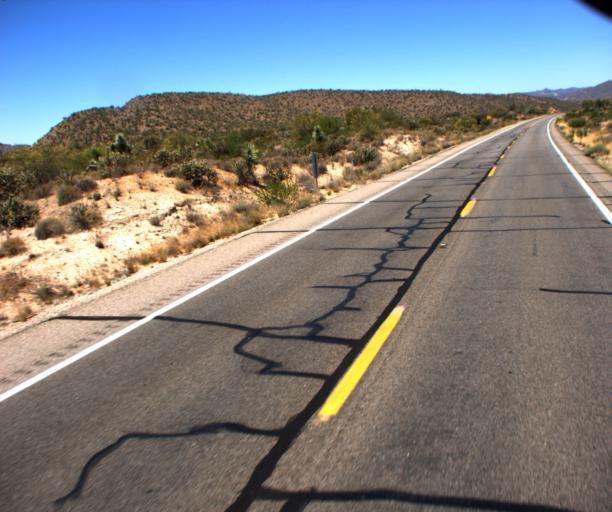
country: US
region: Arizona
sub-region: Yavapai County
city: Bagdad
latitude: 34.3451
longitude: -113.1589
